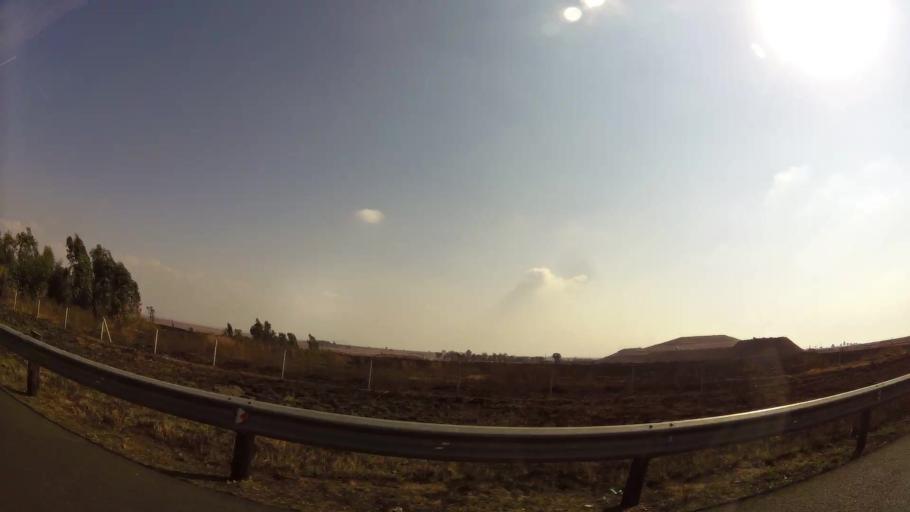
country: ZA
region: Gauteng
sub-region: Ekurhuleni Metropolitan Municipality
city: Springs
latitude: -26.1561
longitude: 28.5229
